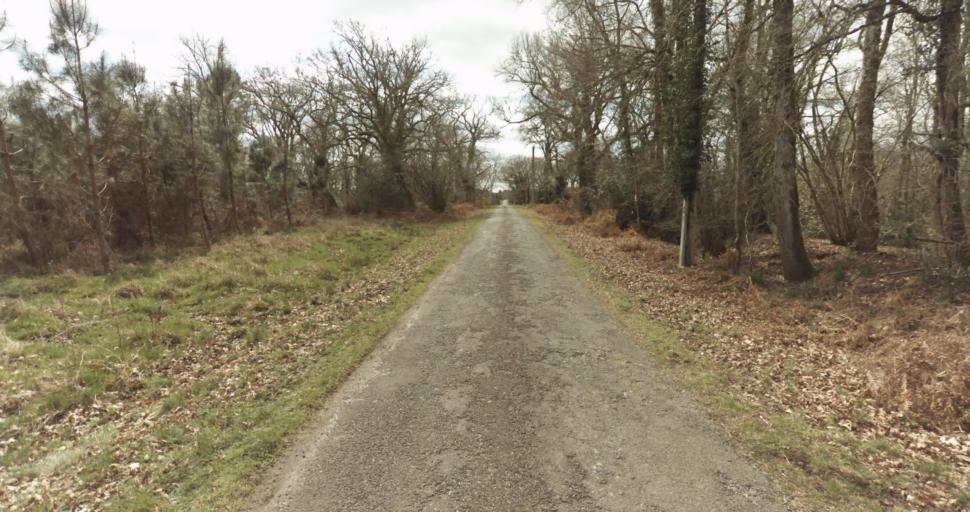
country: FR
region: Aquitaine
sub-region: Departement des Landes
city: Roquefort
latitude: 44.0961
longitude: -0.4396
